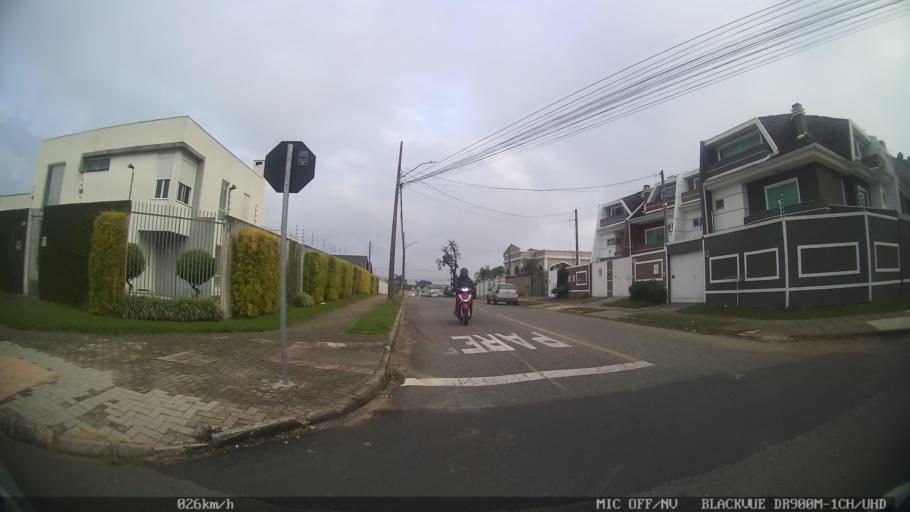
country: BR
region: Parana
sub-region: Almirante Tamandare
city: Almirante Tamandare
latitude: -25.3859
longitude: -49.3368
